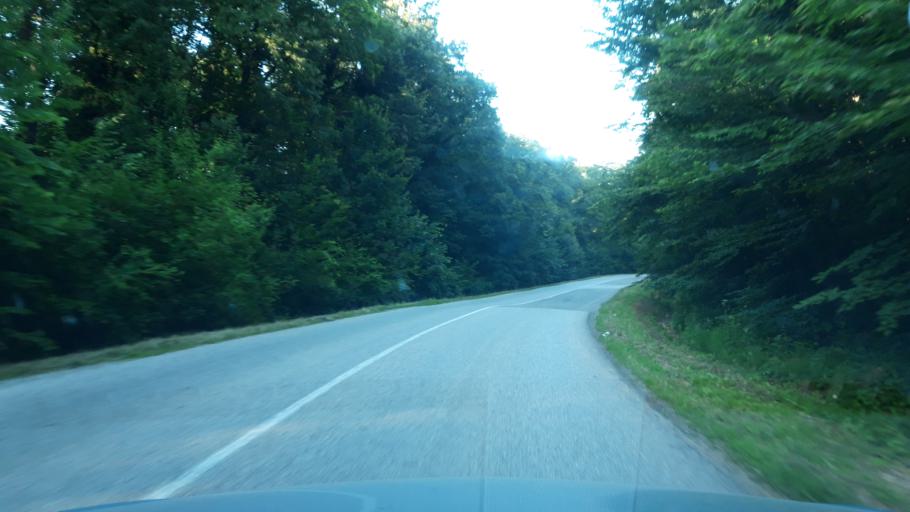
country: RS
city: Glozan
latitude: 45.1537
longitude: 19.5801
